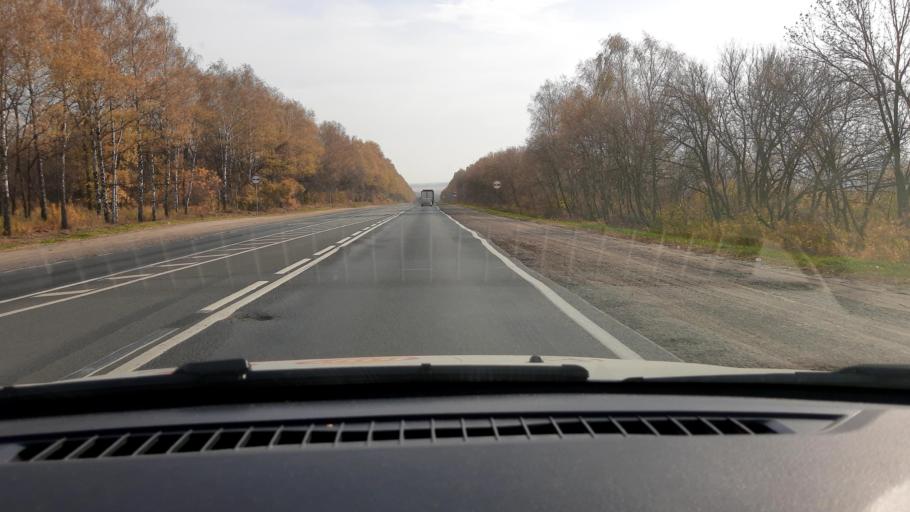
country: RU
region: Nizjnij Novgorod
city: Pamyat' Parizhskoy Kommuny
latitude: 56.0559
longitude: 44.3996
